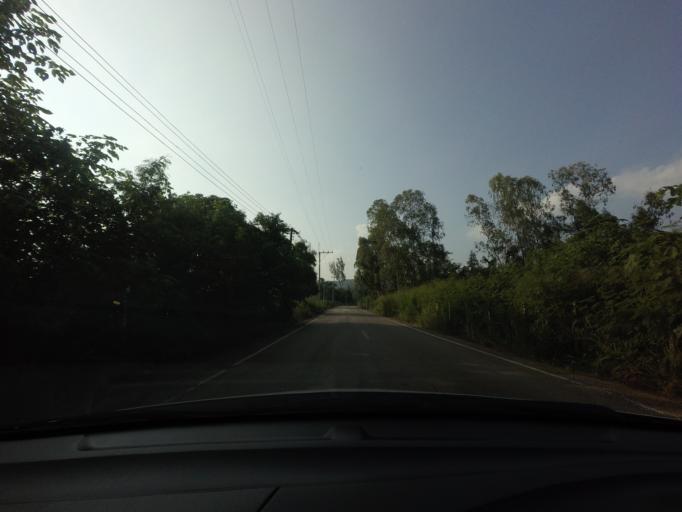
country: TH
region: Nakhon Ratchasima
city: Pak Chong
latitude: 14.5420
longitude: 101.5778
